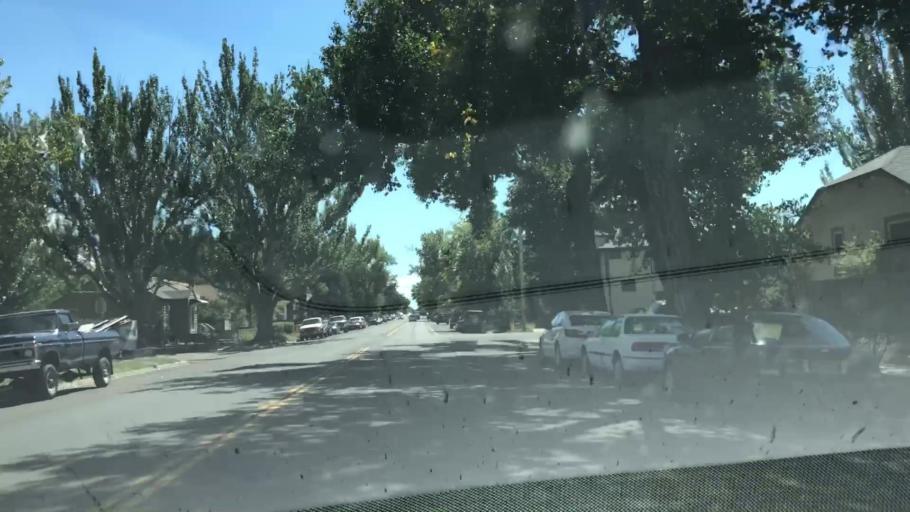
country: US
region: Wyoming
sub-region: Albany County
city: Laramie
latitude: 41.3185
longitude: -105.5849
